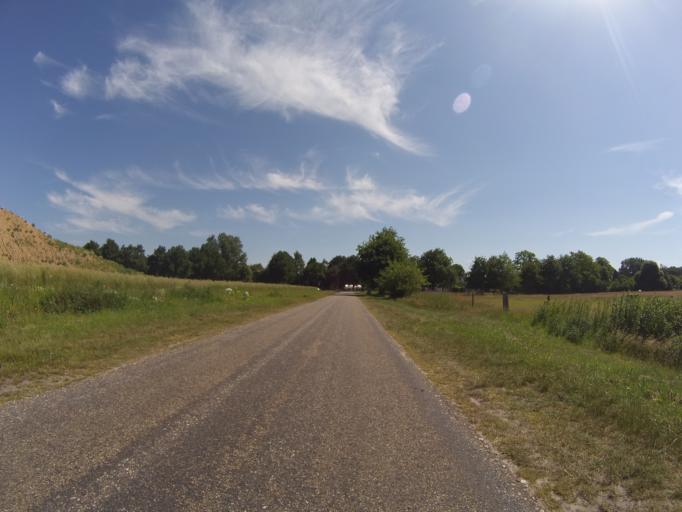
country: NL
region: Drenthe
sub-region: Gemeente Emmen
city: Emmen
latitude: 52.7766
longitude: 6.8827
